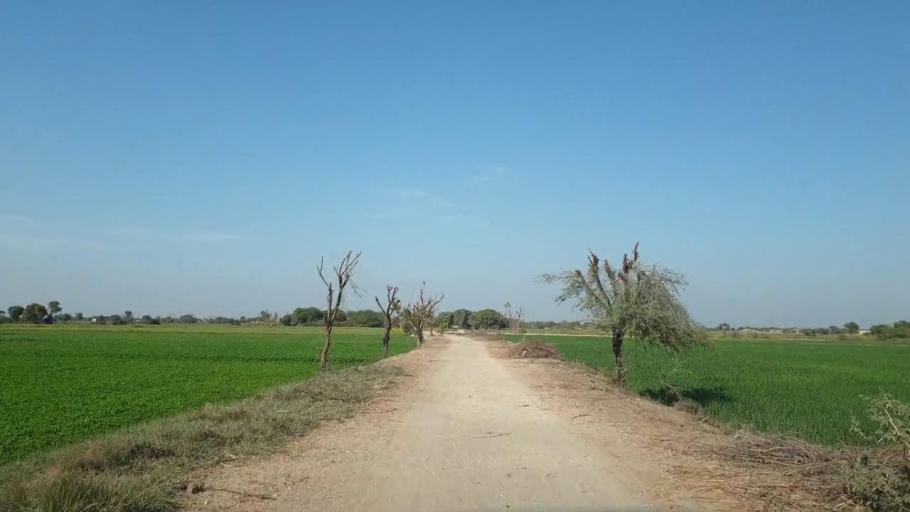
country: PK
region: Sindh
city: Tando Adam
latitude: 25.6788
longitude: 68.6878
